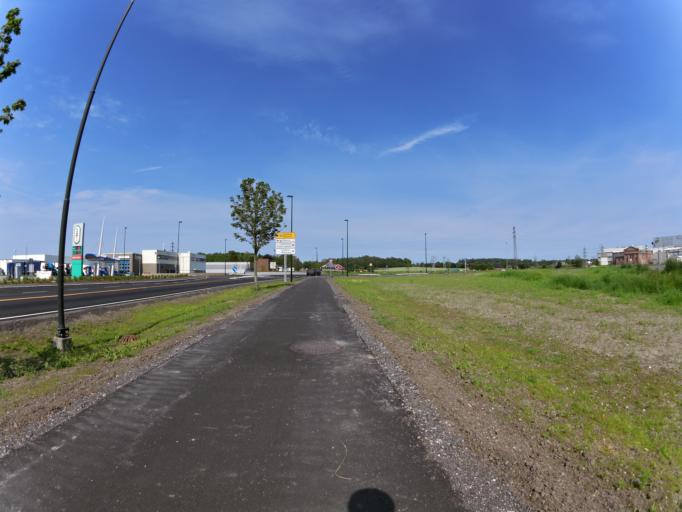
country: NO
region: Ostfold
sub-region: Sarpsborg
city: Sarpsborg
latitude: 59.2647
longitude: 11.1200
